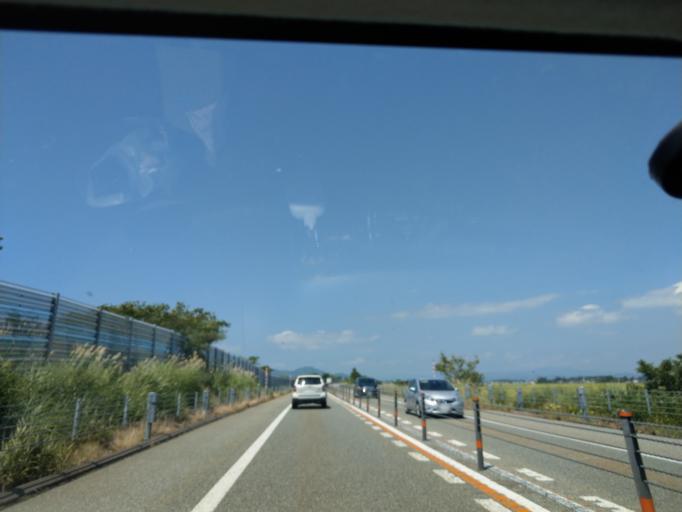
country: JP
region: Akita
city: Omagari
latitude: 39.3778
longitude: 140.4816
